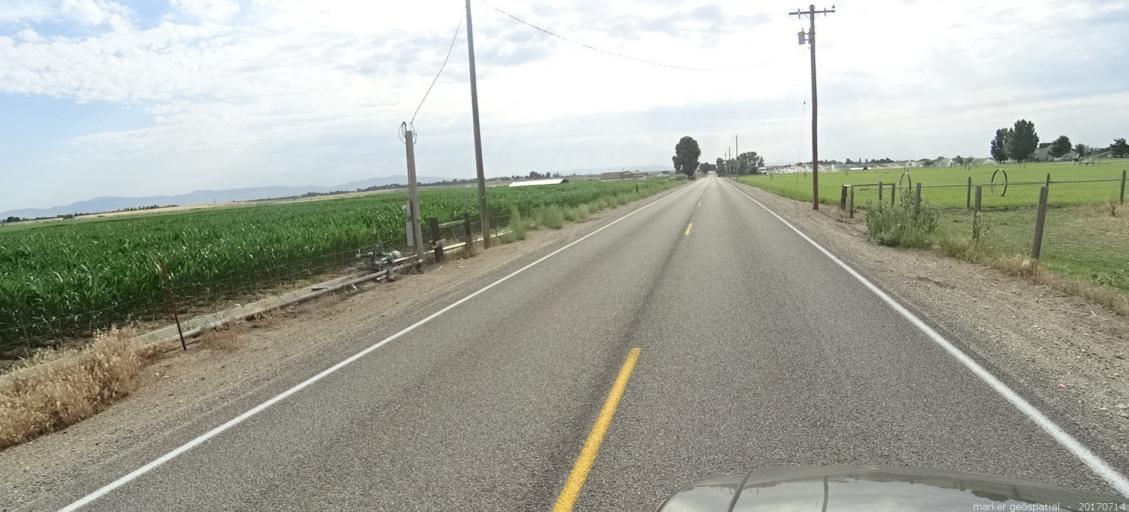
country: US
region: Idaho
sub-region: Ada County
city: Kuna
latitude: 43.4736
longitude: -116.3520
